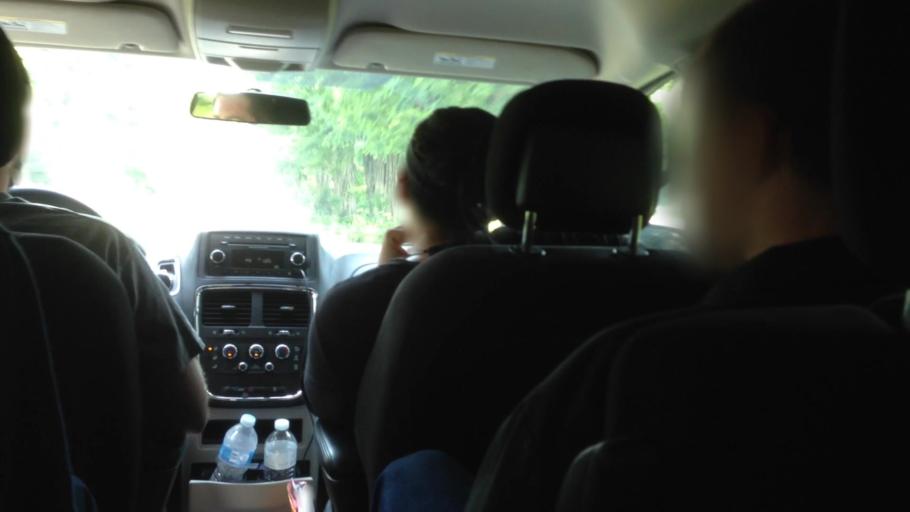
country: US
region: New York
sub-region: Dutchess County
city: Red Hook
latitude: 42.0082
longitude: -73.9113
